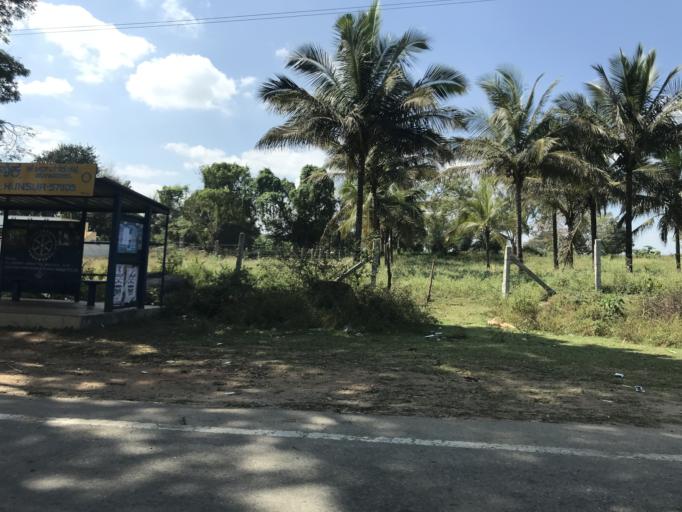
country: IN
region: Karnataka
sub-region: Mysore
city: Hunsur
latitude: 12.3268
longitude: 76.2831
